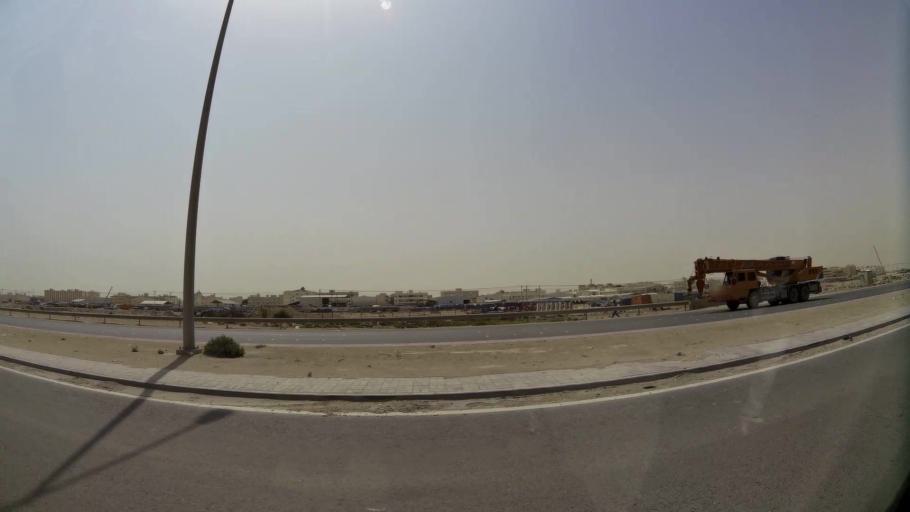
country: QA
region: Baladiyat ar Rayyan
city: Ar Rayyan
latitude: 25.1821
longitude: 51.4203
